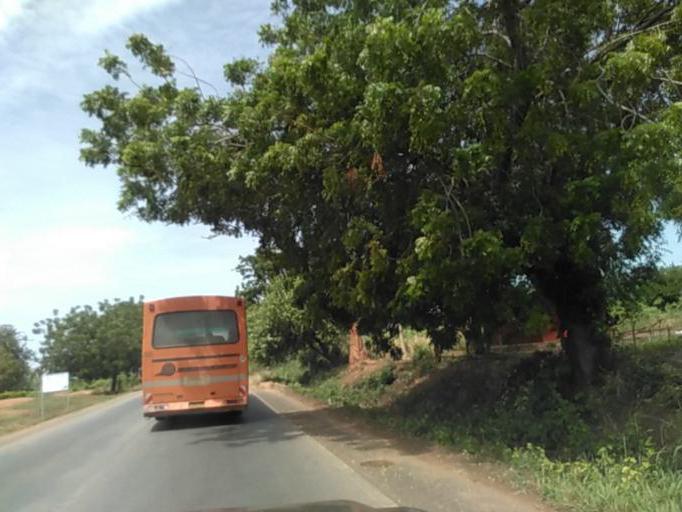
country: GH
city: Akropong
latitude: 6.1953
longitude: 0.0766
